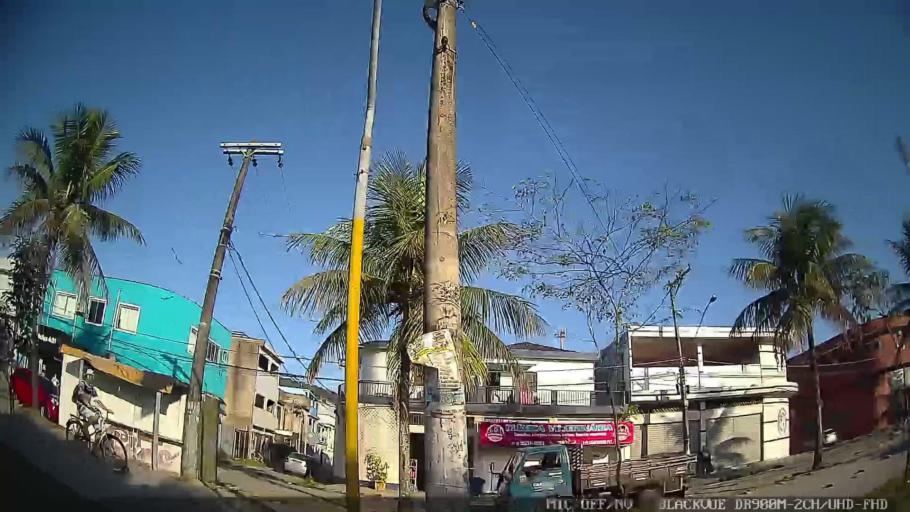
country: BR
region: Sao Paulo
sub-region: Guaruja
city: Guaruja
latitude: -23.9639
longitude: -46.2484
